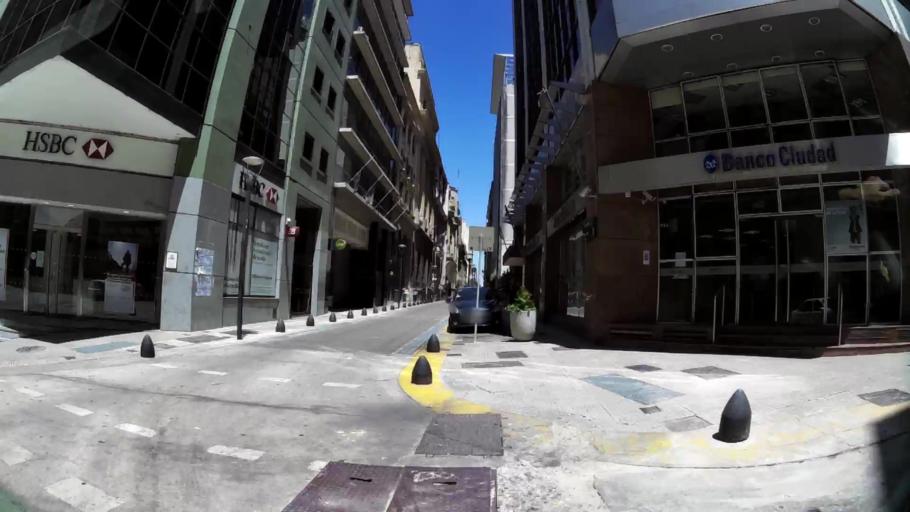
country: AR
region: Buenos Aires F.D.
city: Buenos Aires
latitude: -34.6042
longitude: -58.3705
